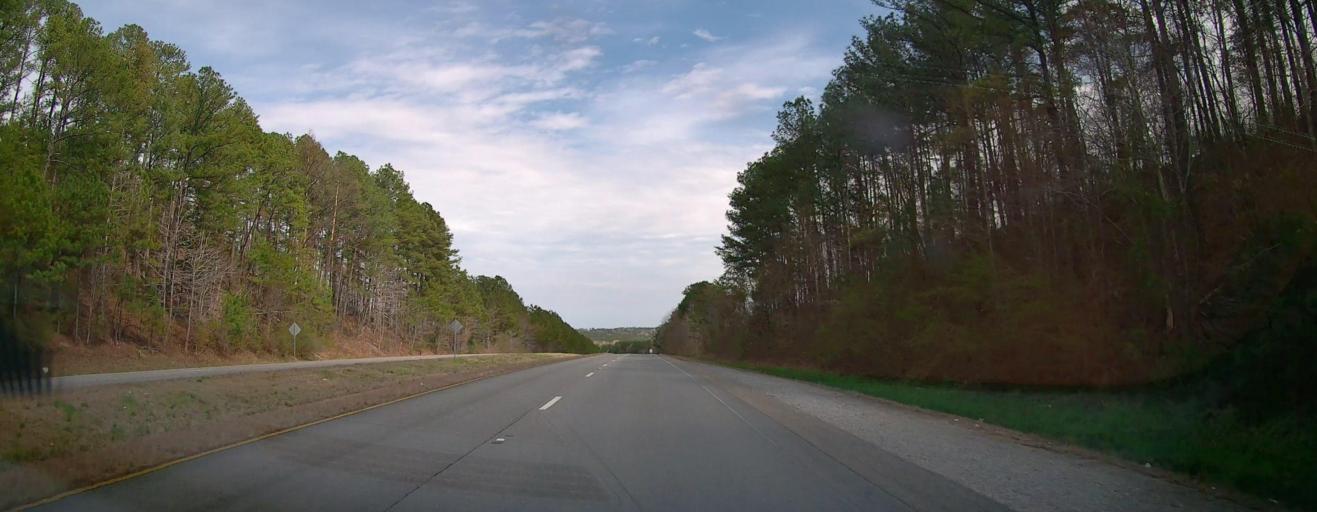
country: US
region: Alabama
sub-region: Marion County
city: Winfield
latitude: 33.9317
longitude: -87.6979
